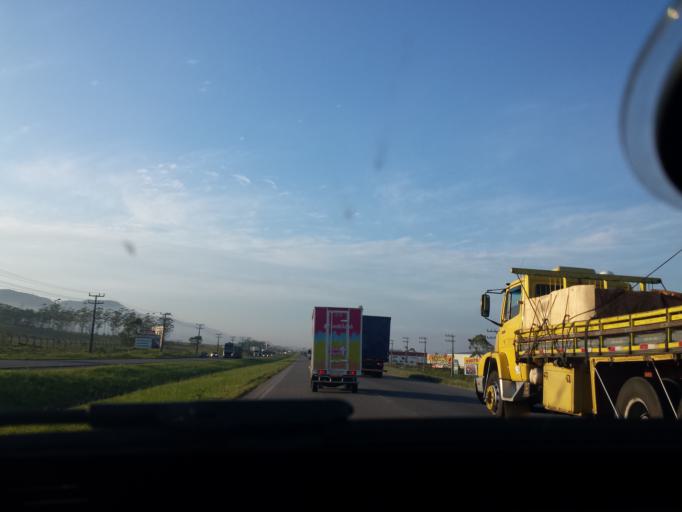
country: BR
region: Santa Catarina
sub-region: Imbituba
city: Imbituba
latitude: -28.1952
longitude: -48.6975
